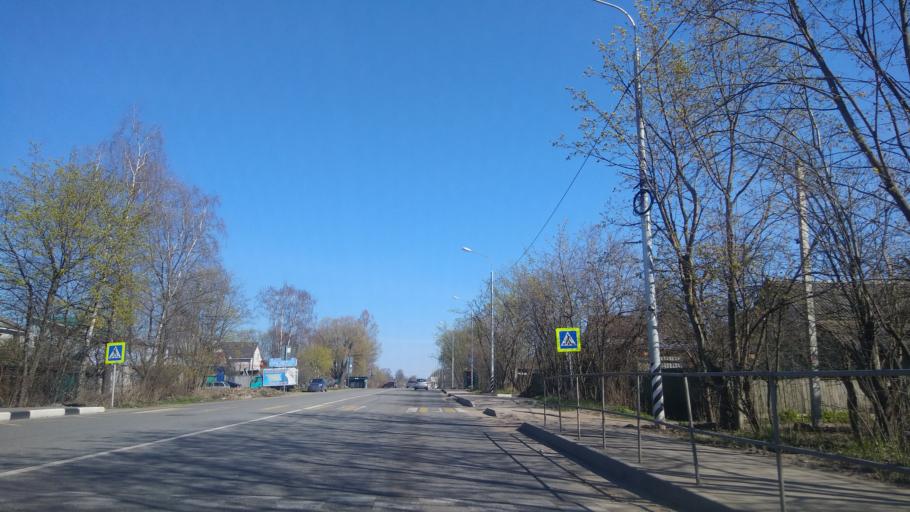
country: RU
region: Moskovskaya
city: Pushkino
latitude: 56.0150
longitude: 37.8719
